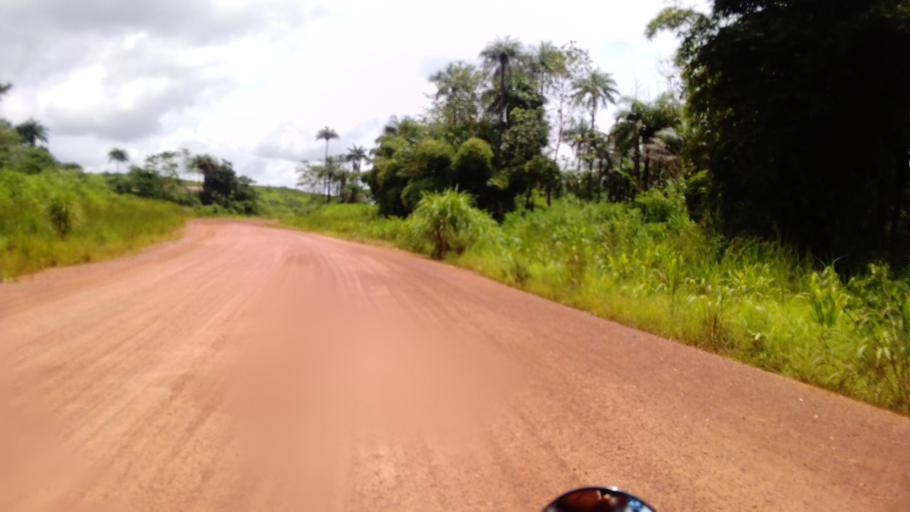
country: SL
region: Northern Province
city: Makeni
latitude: 9.0773
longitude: -12.1823
